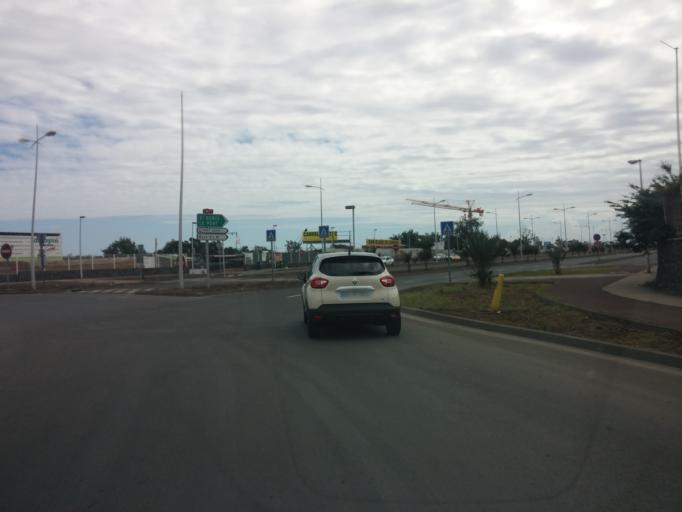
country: RE
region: Reunion
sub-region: Reunion
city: Le Port
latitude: -20.9652
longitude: 55.2949
